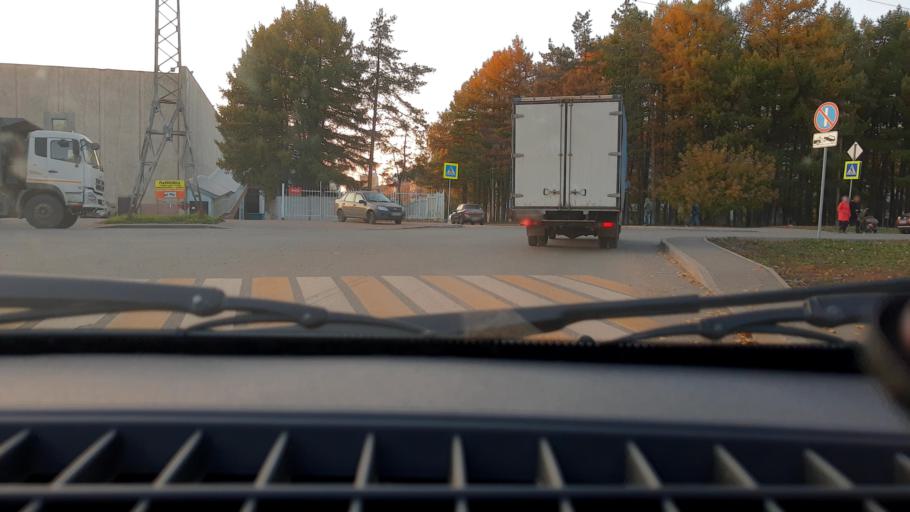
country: RU
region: Bashkortostan
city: Ufa
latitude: 54.7655
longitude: 56.0233
